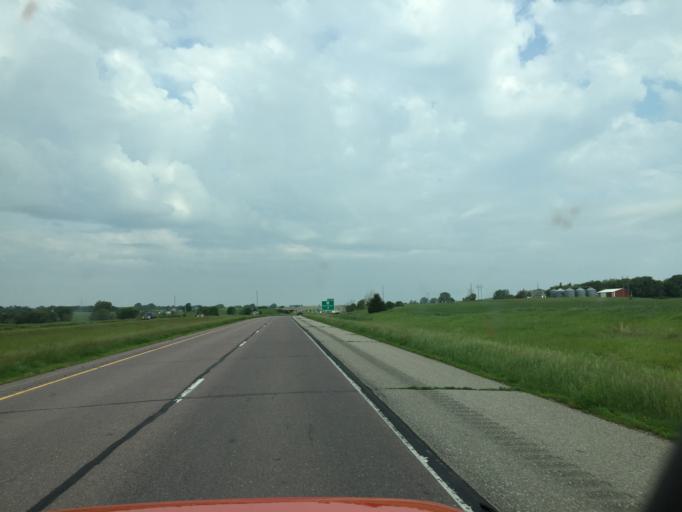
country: US
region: Minnesota
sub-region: Martin County
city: Fairmont
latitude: 43.6793
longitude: -94.4831
